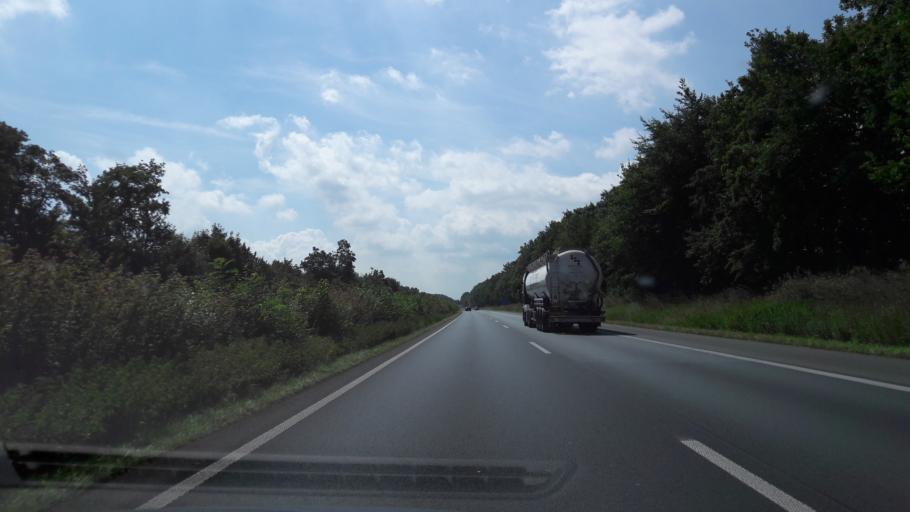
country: DE
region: North Rhine-Westphalia
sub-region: Regierungsbezirk Munster
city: Ascheberg
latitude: 51.7588
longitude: 7.6433
